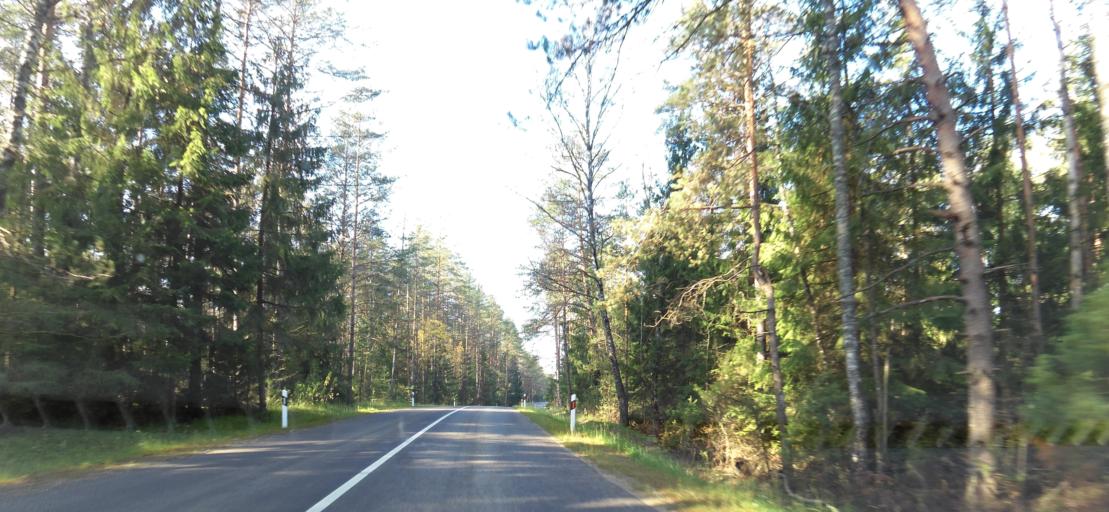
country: LT
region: Vilnius County
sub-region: Trakai
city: Rudiskes
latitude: 54.5100
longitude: 24.9074
